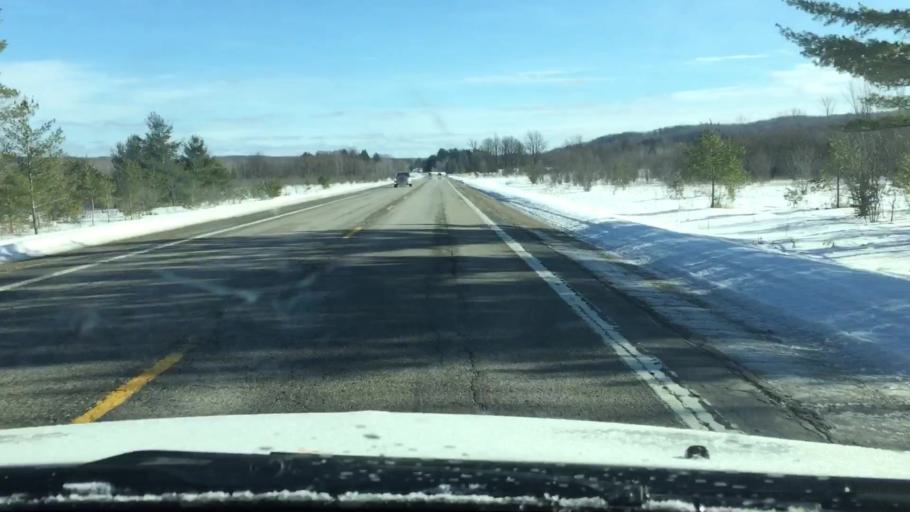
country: US
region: Michigan
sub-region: Charlevoix County
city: East Jordan
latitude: 45.1032
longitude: -85.1192
